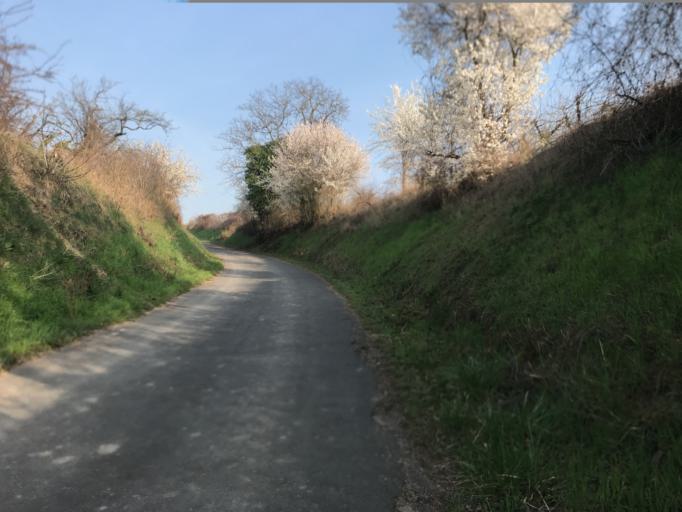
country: DE
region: Rheinland-Pfalz
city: Wackernheim
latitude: 49.9891
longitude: 8.1197
